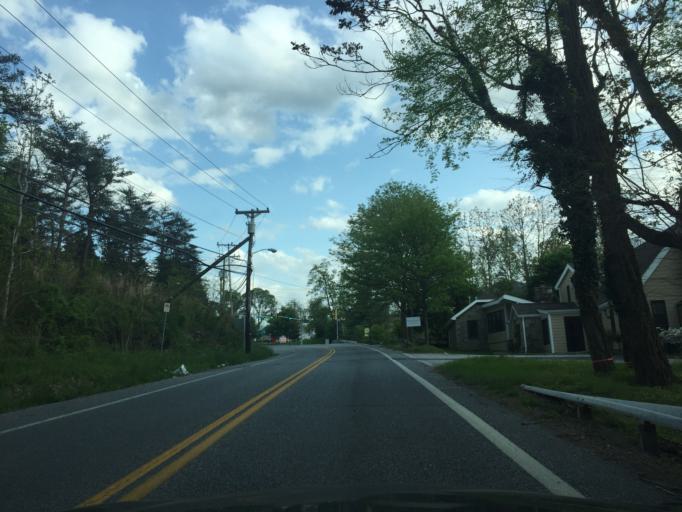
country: US
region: Maryland
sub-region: Baltimore County
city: Mays Chapel
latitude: 39.3866
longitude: -76.6593
